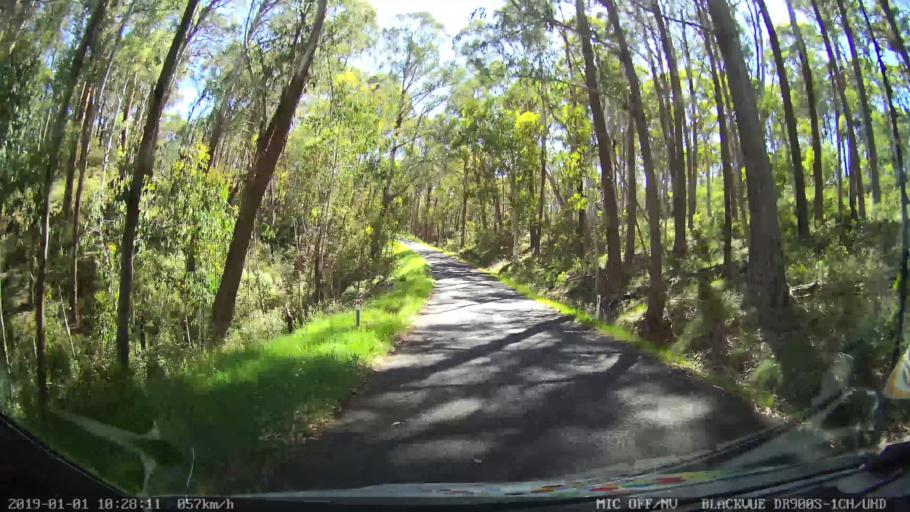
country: AU
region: New South Wales
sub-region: Snowy River
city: Jindabyne
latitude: -36.0618
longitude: 148.2385
